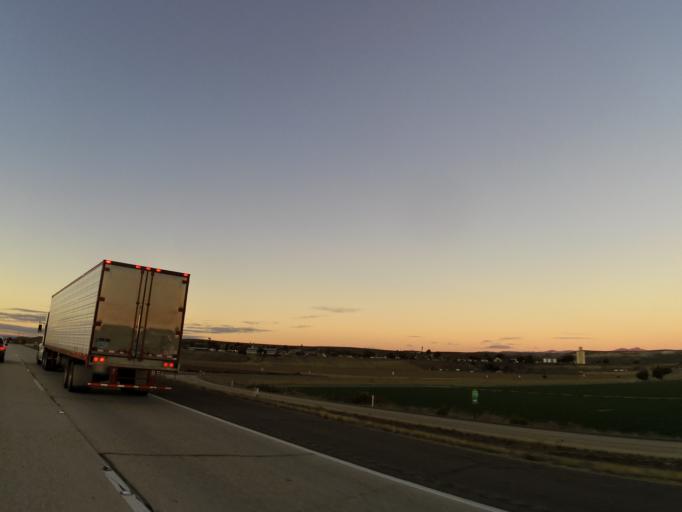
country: US
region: California
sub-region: Monterey County
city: King City
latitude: 36.1207
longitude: -121.0222
